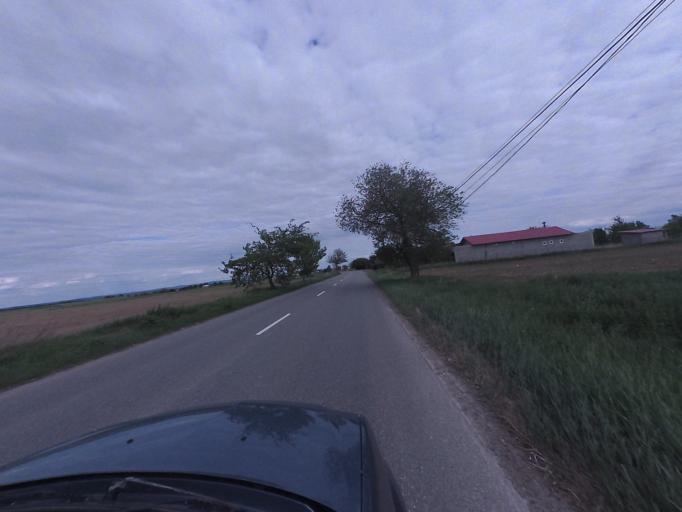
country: RO
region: Neamt
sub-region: Comuna Trifesti
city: Miron Costin
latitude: 46.9572
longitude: 26.8037
